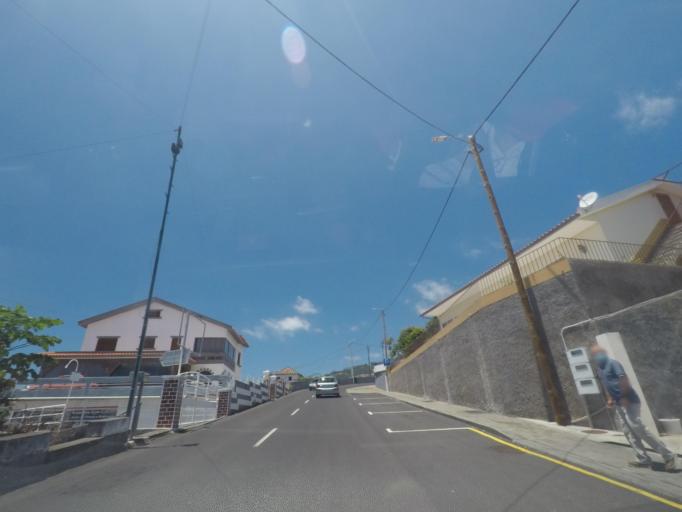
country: PT
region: Madeira
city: Calheta
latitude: 32.7245
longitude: -17.1812
